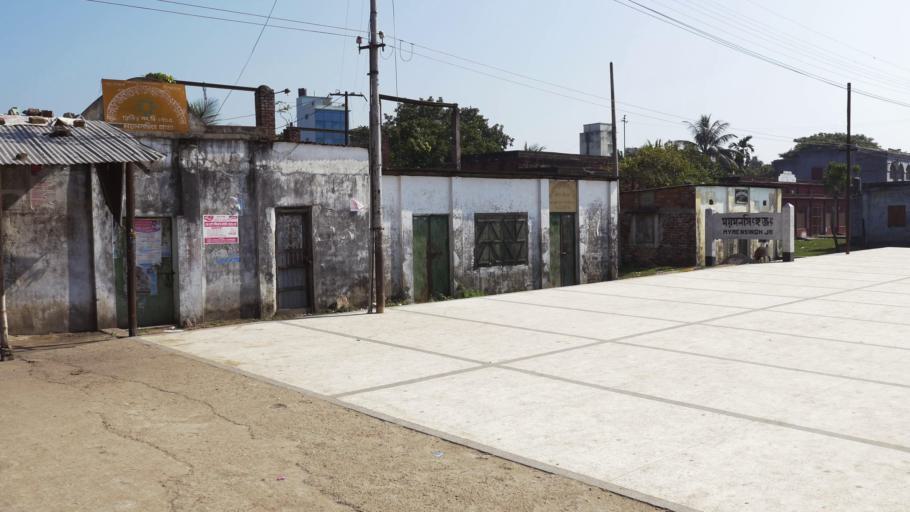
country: BD
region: Dhaka
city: Mymensingh
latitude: 24.6357
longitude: 90.4590
